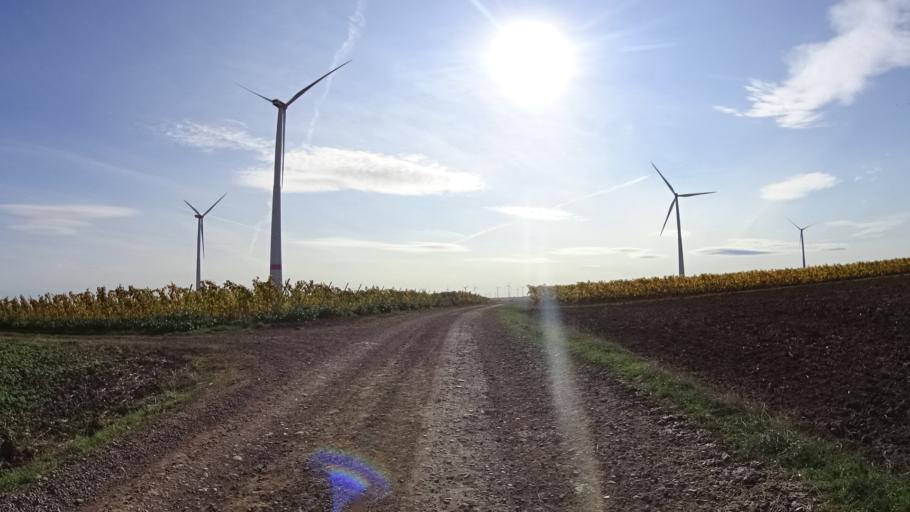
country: DE
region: Rheinland-Pfalz
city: Gau-Bickelheim
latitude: 49.8133
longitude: 8.0197
